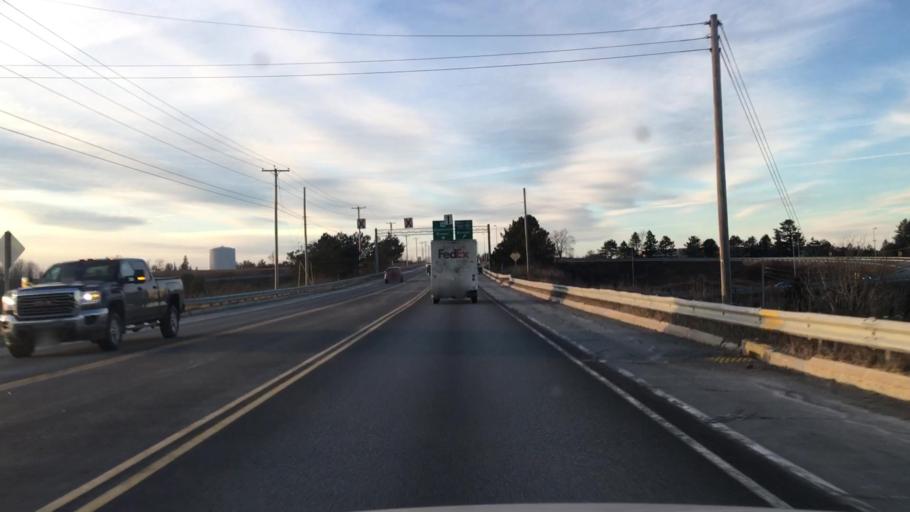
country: US
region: Maine
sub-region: Penobscot County
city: Holden
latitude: 44.7705
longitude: -68.7195
